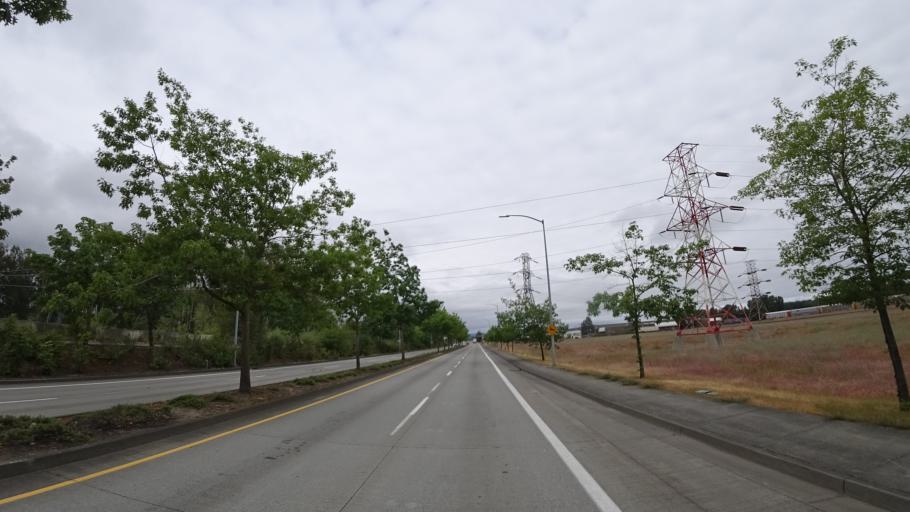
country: US
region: Washington
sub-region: Clark County
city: Vancouver
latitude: 45.6209
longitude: -122.7279
